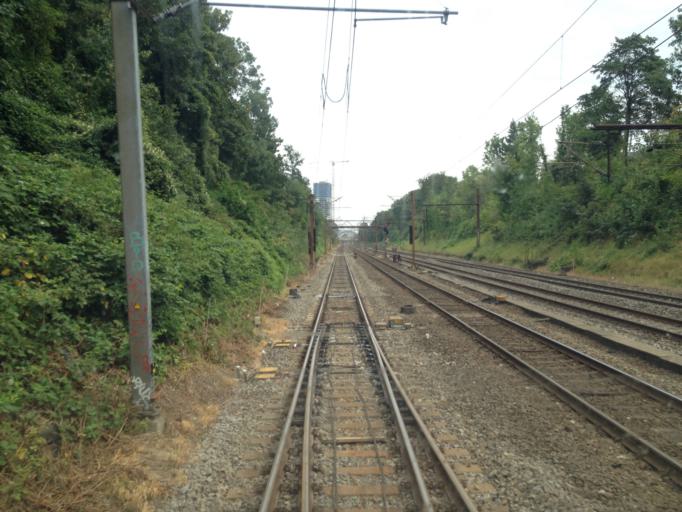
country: DK
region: Capital Region
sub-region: Frederiksberg Kommune
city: Frederiksberg
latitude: 55.6638
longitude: 12.5203
